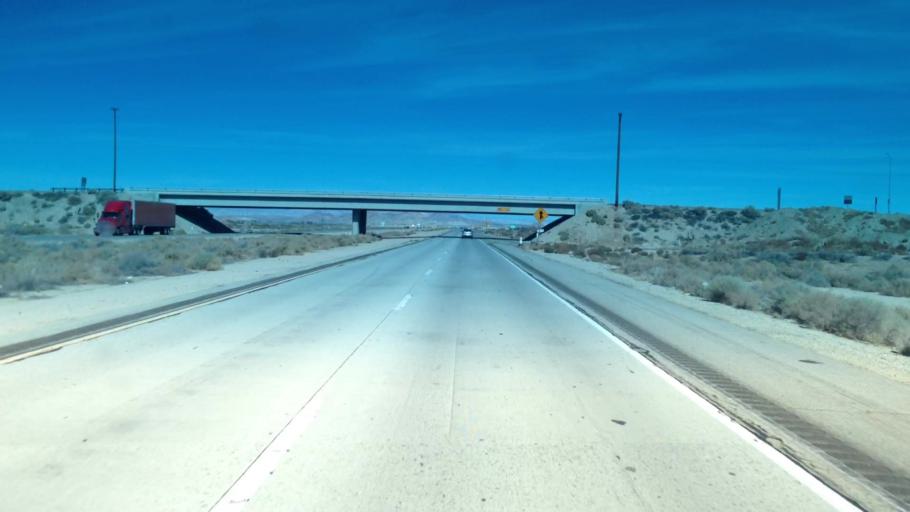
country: US
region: California
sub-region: Los Angeles County
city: Lancaster
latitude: 34.7754
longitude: -118.1705
